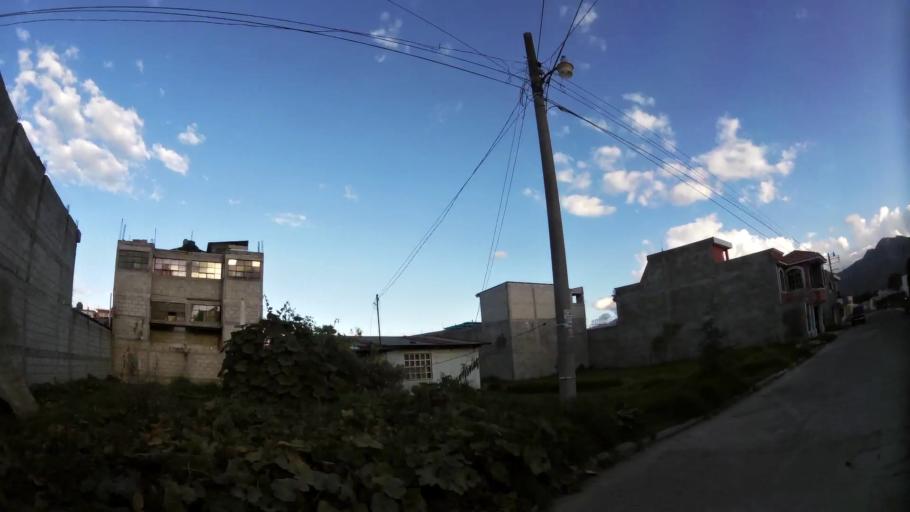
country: GT
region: Quetzaltenango
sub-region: Municipio de La Esperanza
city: La Esperanza
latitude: 14.8597
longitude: -91.5367
